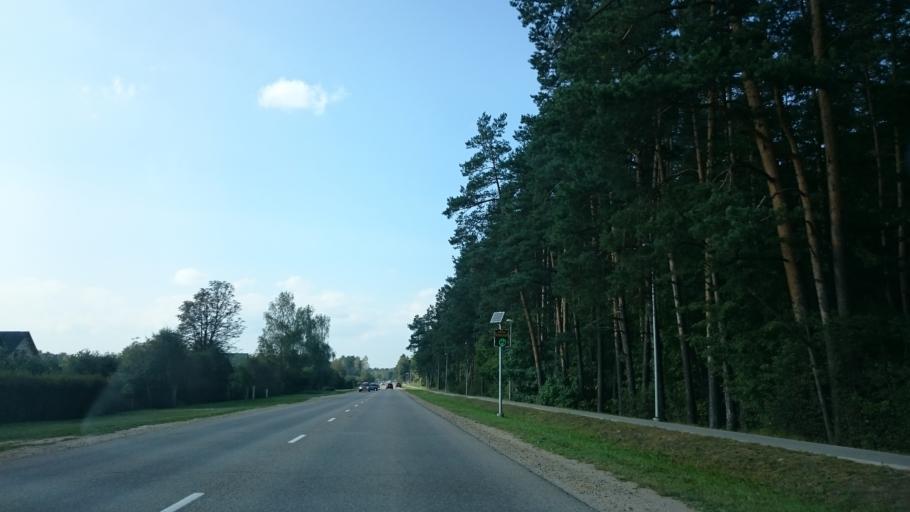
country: LV
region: Stopini
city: Ulbroka
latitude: 56.9375
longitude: 24.3006
